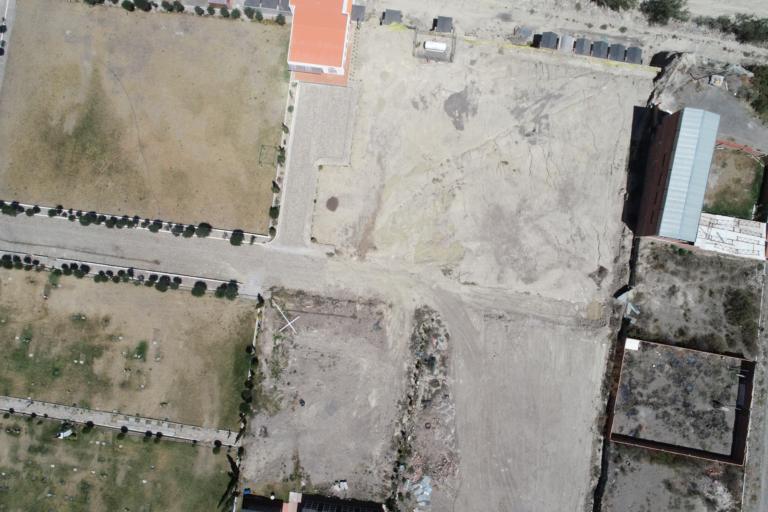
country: BO
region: La Paz
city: La Paz
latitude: -16.6177
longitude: -68.0587
